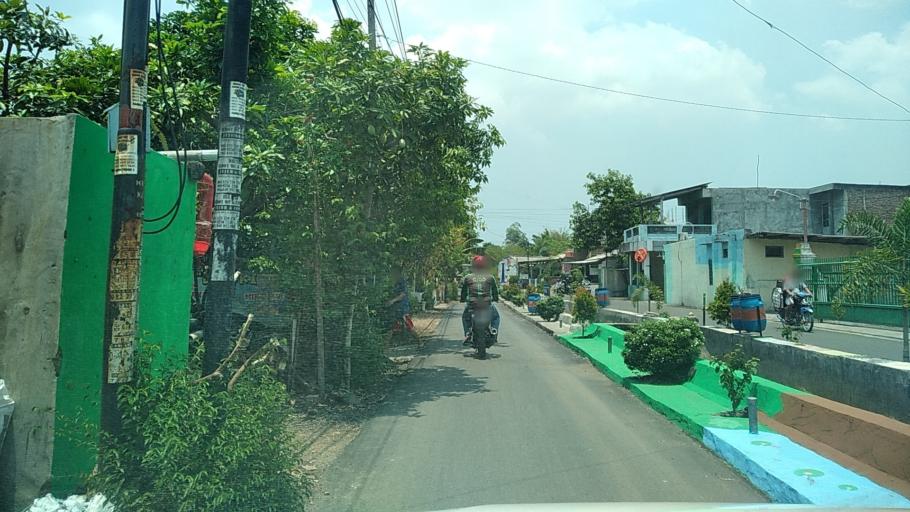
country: ID
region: Central Java
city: Semarang
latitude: -7.0019
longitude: 110.4416
